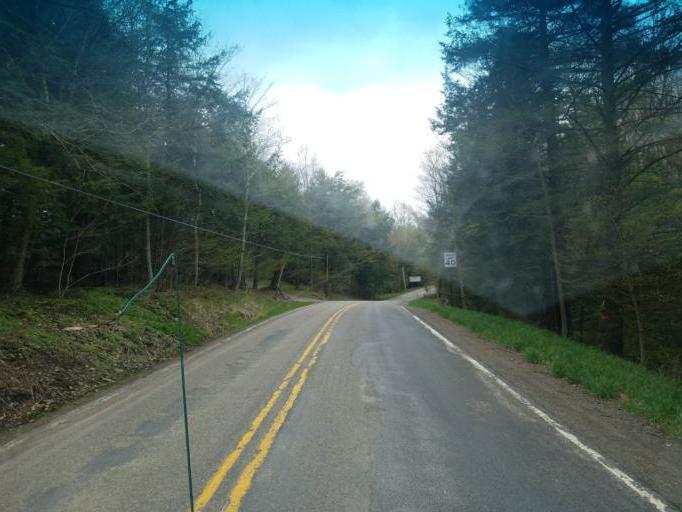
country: US
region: Pennsylvania
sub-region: Tioga County
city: Wellsboro
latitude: 41.6968
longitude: -77.4352
